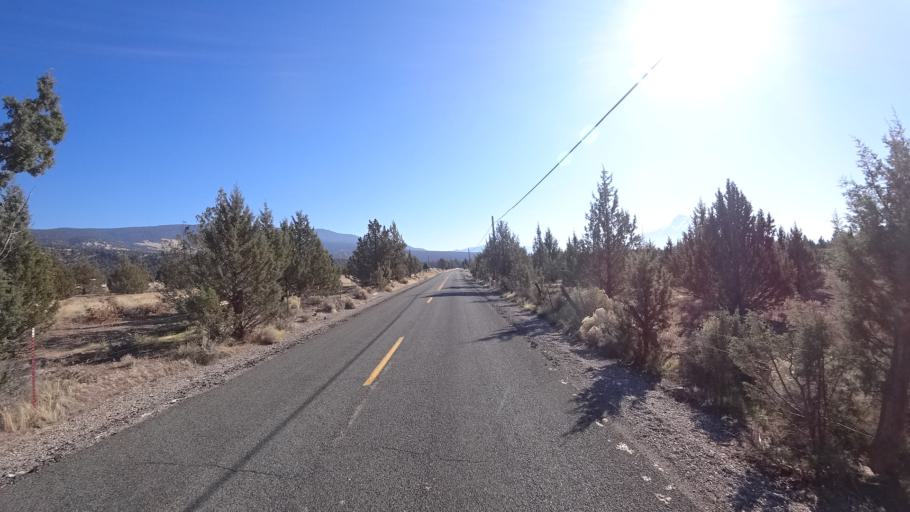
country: US
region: California
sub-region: Siskiyou County
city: Montague
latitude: 41.6435
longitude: -122.3511
